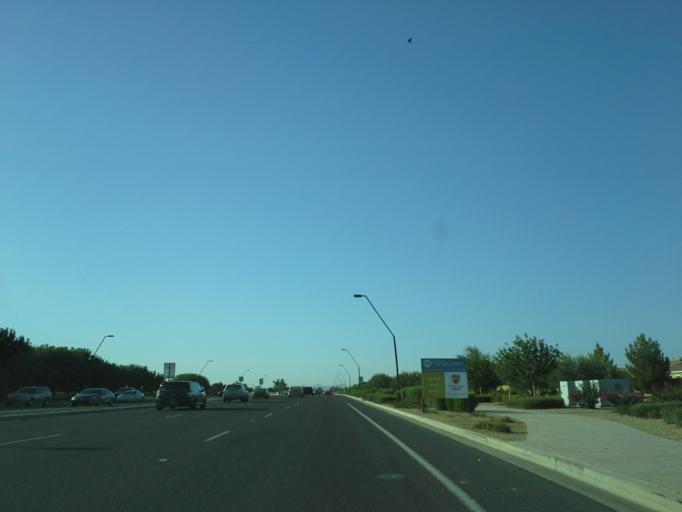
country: US
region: Arizona
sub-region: Maricopa County
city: Queen Creek
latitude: 33.2271
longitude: -111.6343
